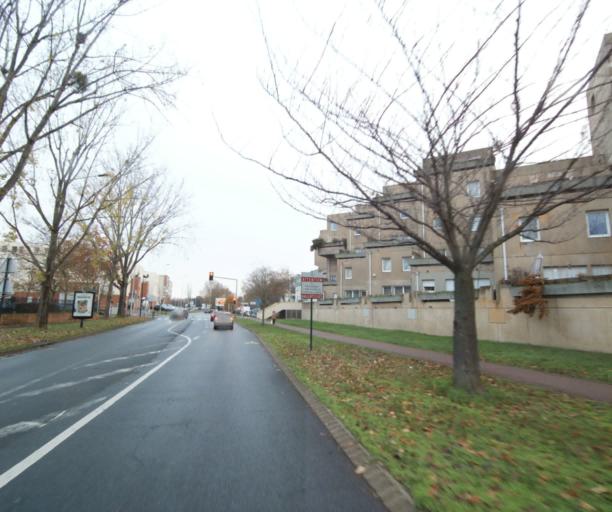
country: FR
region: Ile-de-France
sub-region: Departement de l'Essonne
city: Ris-Orangis
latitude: 48.6362
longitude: 2.4257
